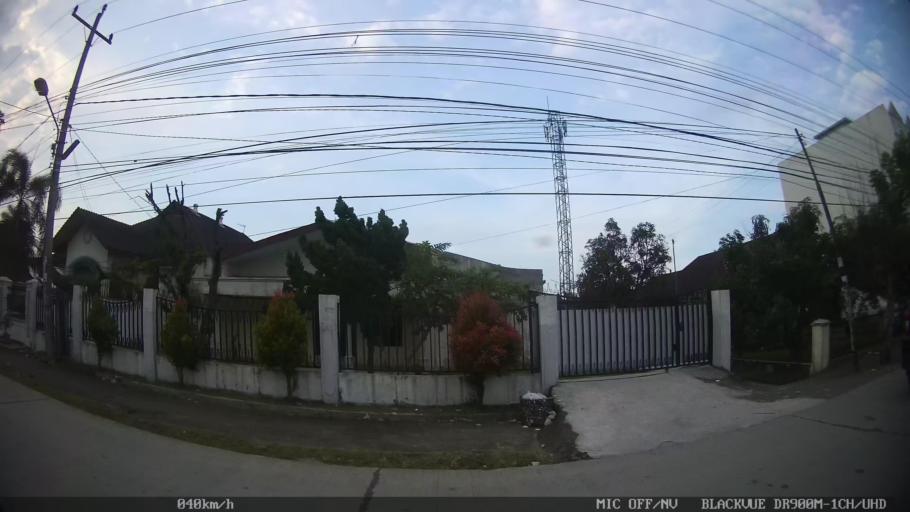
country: ID
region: North Sumatra
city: Medan
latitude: 3.6091
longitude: 98.7062
